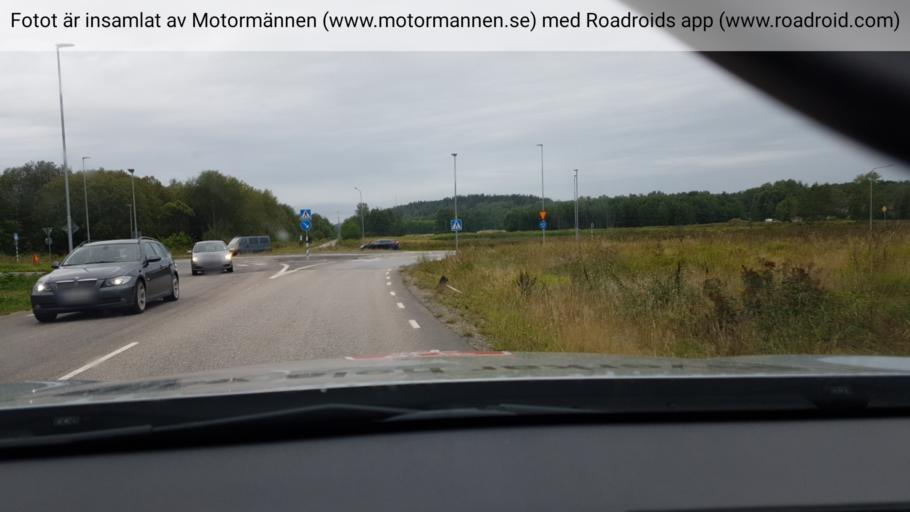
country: SE
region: Vaestra Goetaland
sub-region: Trollhattan
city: Trollhattan
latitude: 58.3139
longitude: 12.2998
